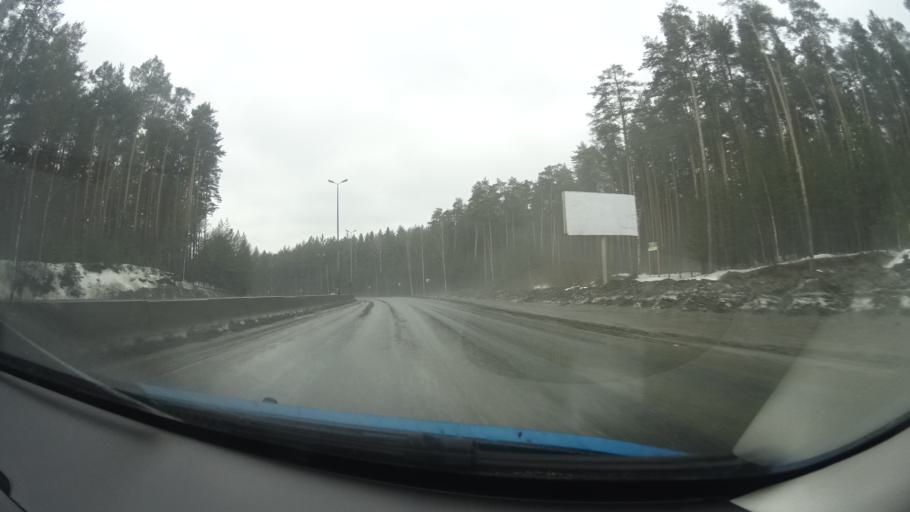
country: RU
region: Perm
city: Perm
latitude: 58.0477
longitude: 56.1839
